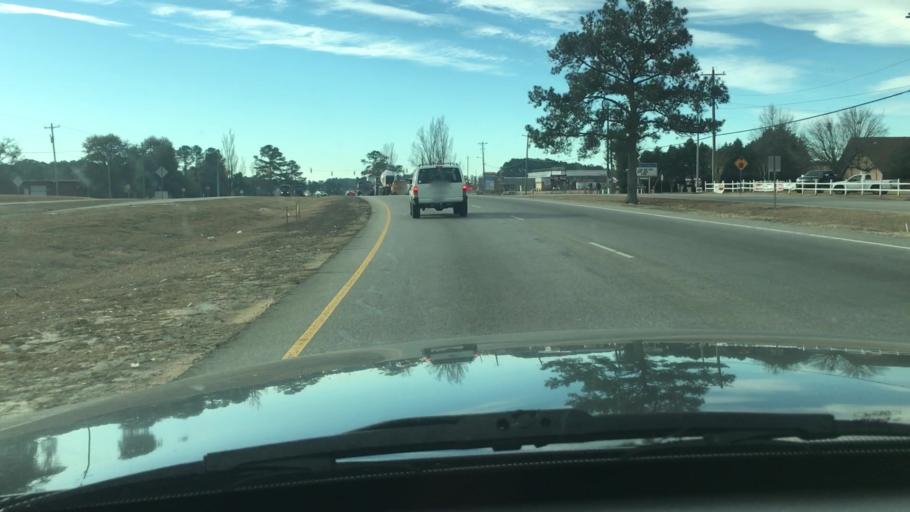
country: US
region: North Carolina
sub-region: Cumberland County
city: Fayetteville
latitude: 35.0060
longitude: -78.8991
